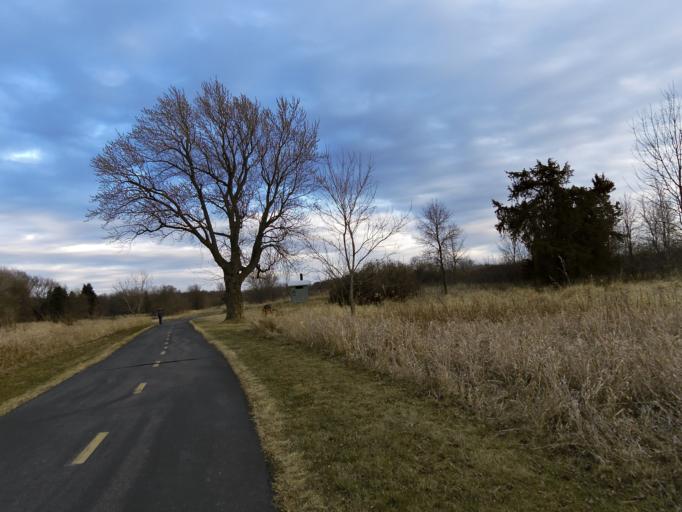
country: US
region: Minnesota
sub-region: Scott County
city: Prior Lake
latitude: 44.6929
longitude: -93.4032
